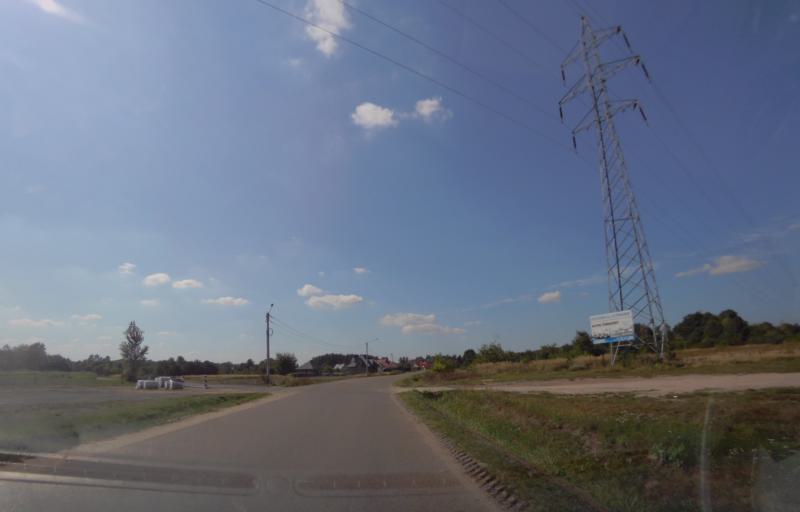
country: PL
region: Subcarpathian Voivodeship
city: Nowa Sarzyna
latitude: 50.3099
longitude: 22.3351
